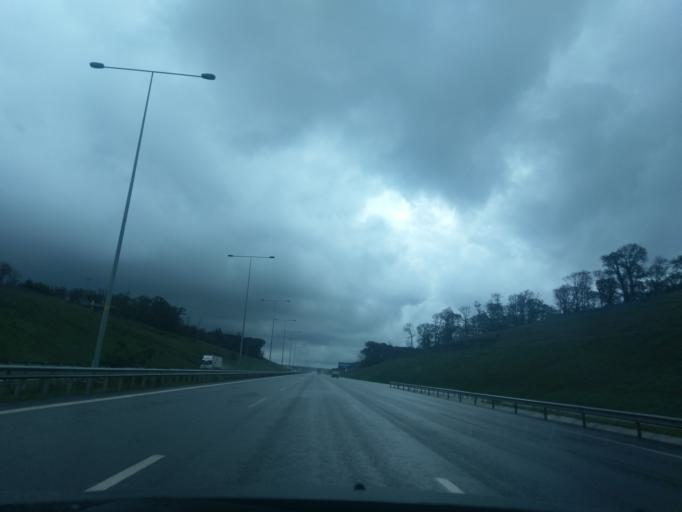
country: TR
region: Istanbul
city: Kemerburgaz
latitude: 41.2354
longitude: 28.8909
